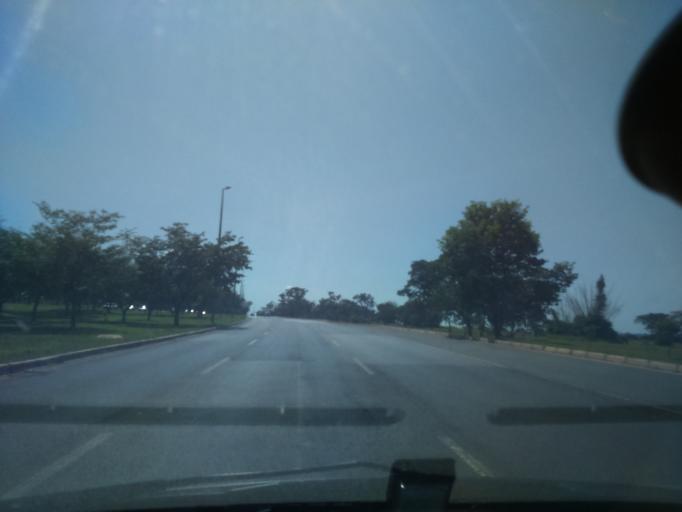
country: BR
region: Federal District
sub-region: Brasilia
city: Brasilia
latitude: -15.8130
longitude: -47.8666
